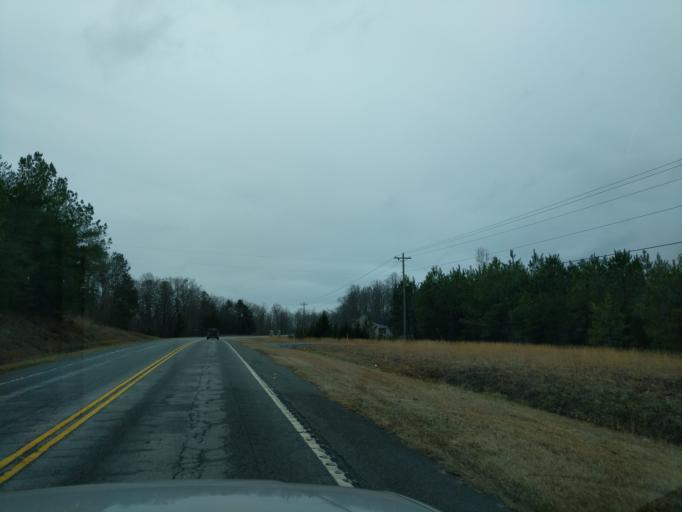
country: US
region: South Carolina
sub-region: Oconee County
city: Walhalla
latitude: 34.8394
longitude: -83.0376
